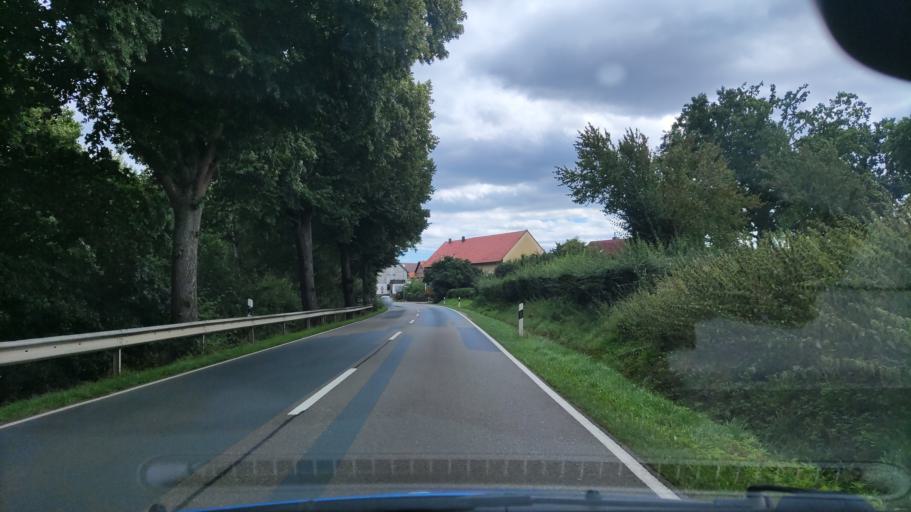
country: DE
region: Lower Saxony
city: Einbeck
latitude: 51.8273
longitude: 9.8109
